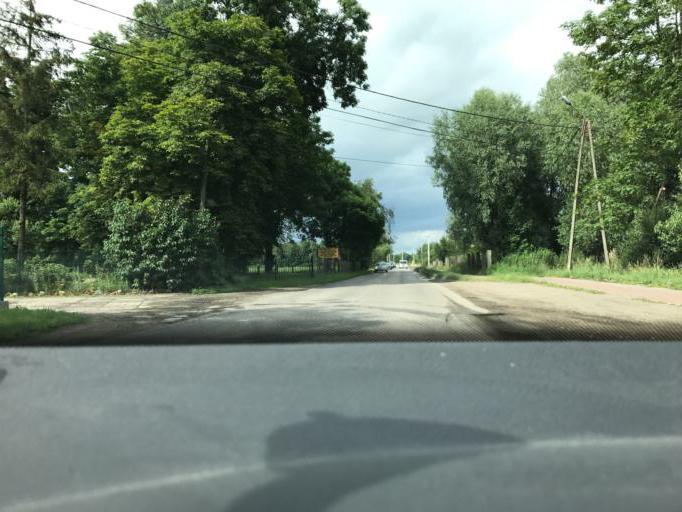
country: PL
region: Pomeranian Voivodeship
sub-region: Powiat gdanski
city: Pruszcz Gdanski
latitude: 54.2962
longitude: 18.7205
